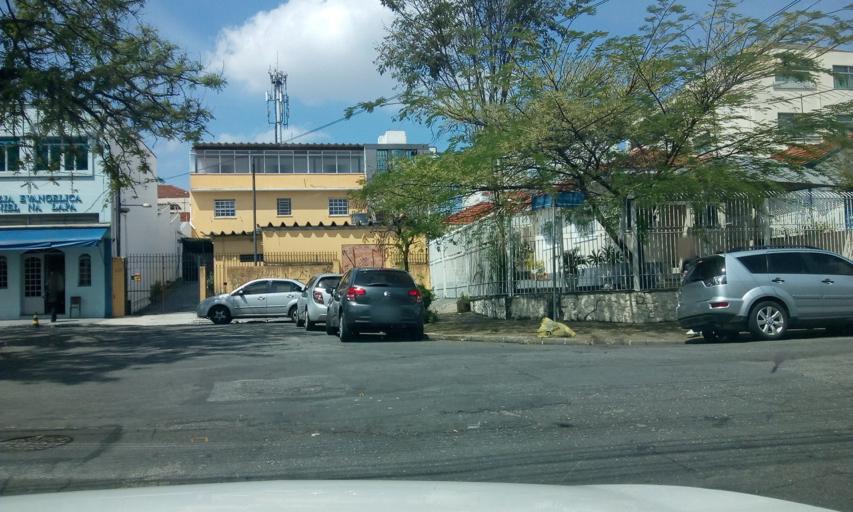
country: BR
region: Sao Paulo
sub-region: Sao Paulo
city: Sao Paulo
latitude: -23.5212
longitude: -46.7097
